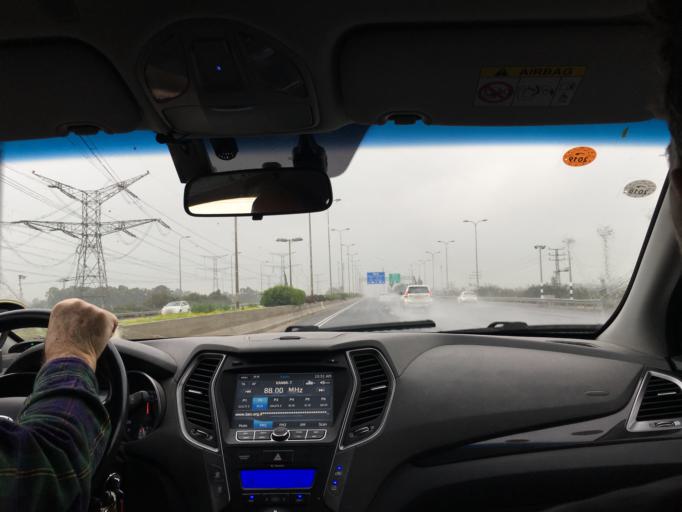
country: IL
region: Central District
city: Petah Tiqwa
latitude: 32.1223
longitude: 34.8962
